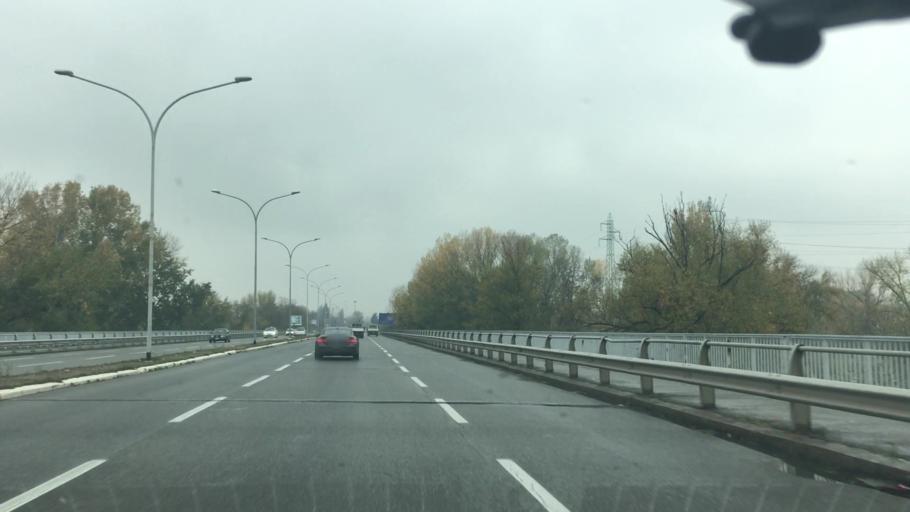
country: IT
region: Emilia-Romagna
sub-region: Provincia di Bologna
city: Casalecchio di Reno
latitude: 44.5052
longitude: 11.2902
